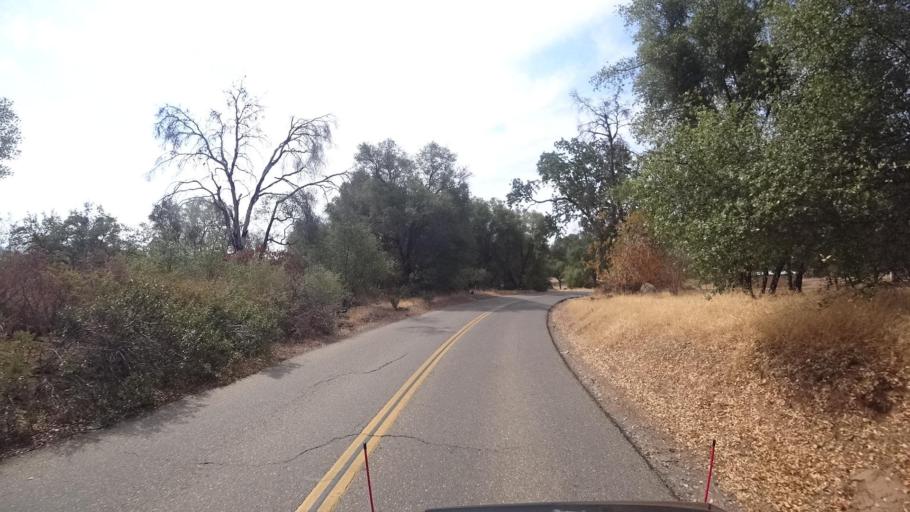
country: US
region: California
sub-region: Mariposa County
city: Midpines
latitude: 37.4870
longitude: -119.9052
